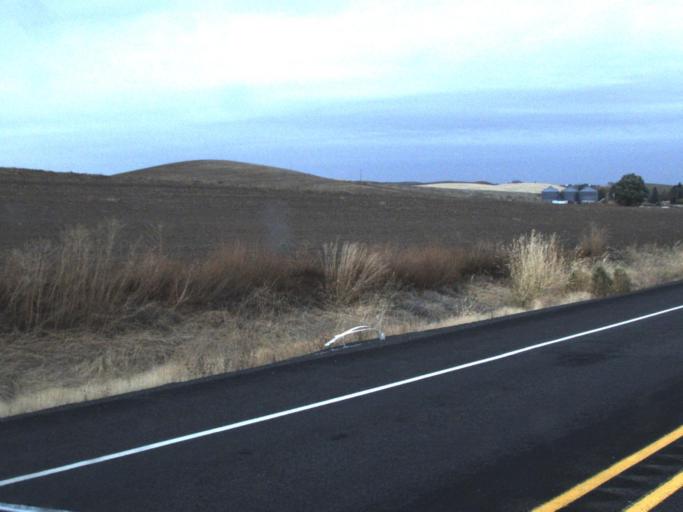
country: US
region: Washington
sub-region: Whitman County
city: Pullman
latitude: 46.6778
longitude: -117.1945
